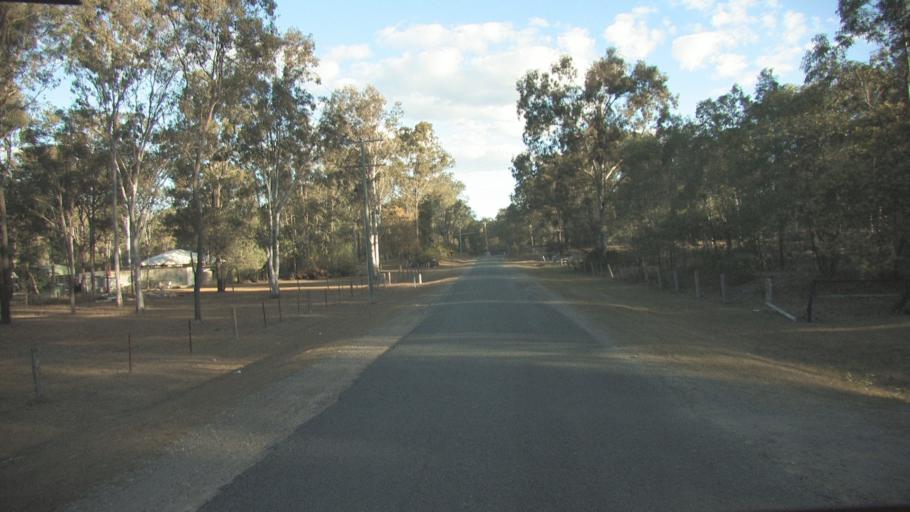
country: AU
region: Queensland
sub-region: Logan
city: Cedar Vale
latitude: -27.8540
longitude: 153.0888
